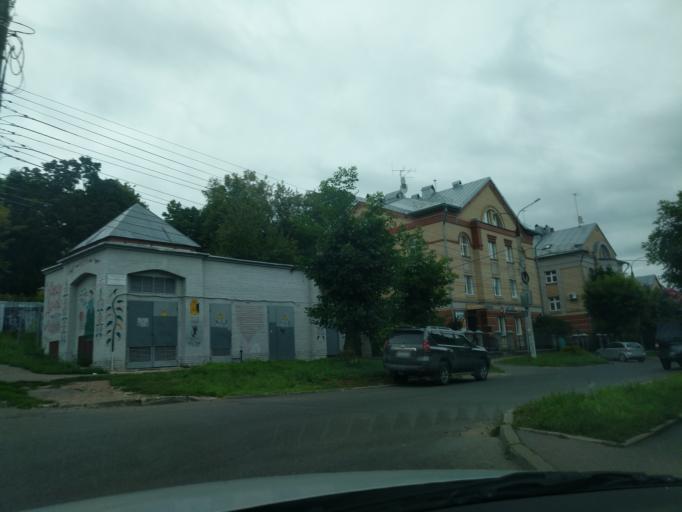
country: RU
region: Kirov
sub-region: Kirovo-Chepetskiy Rayon
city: Kirov
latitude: 58.6002
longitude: 49.6726
